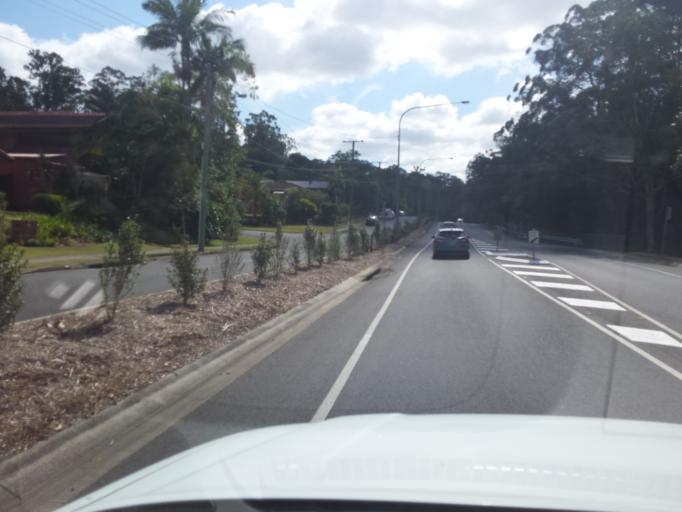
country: AU
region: Queensland
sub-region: Brisbane
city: Everton Park
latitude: -27.3814
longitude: 152.9741
